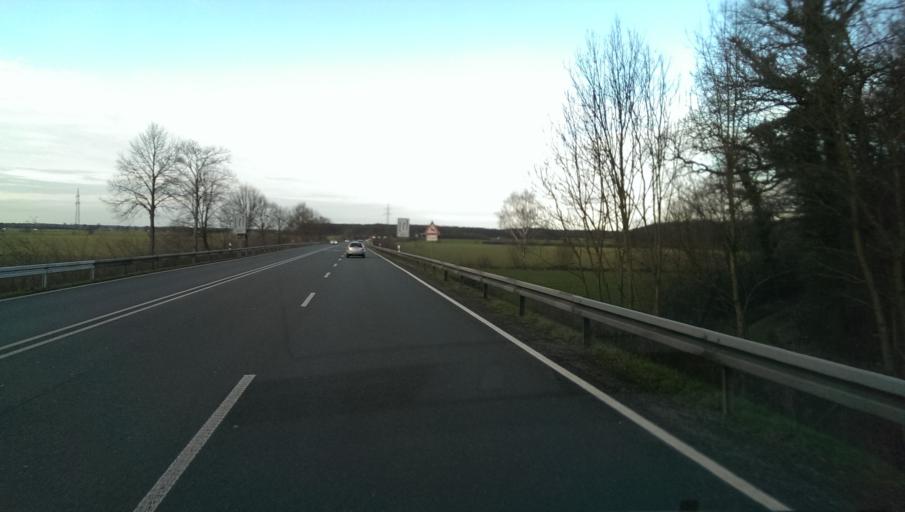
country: DE
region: North Rhine-Westphalia
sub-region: Regierungsbezirk Detmold
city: Salzkotten
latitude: 51.6717
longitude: 8.6523
